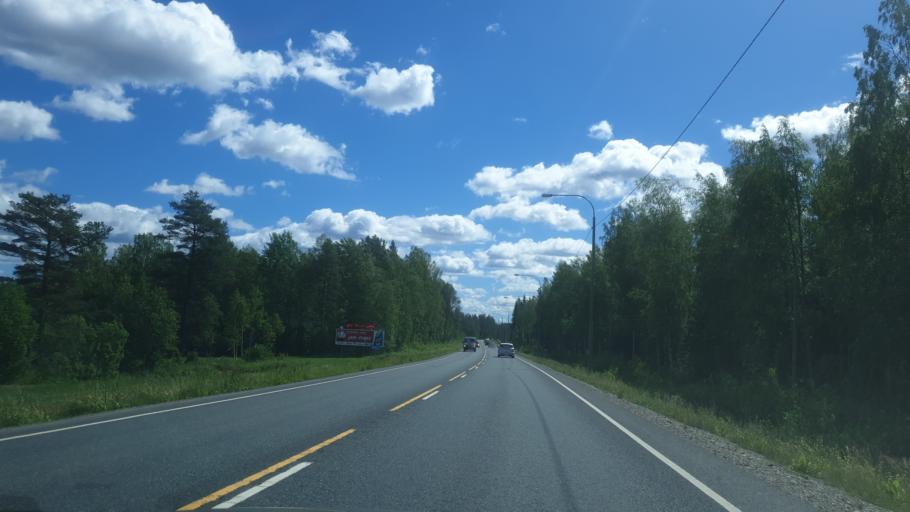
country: FI
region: Northern Savo
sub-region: Varkaus
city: Leppaevirta
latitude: 62.5396
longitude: 27.6359
